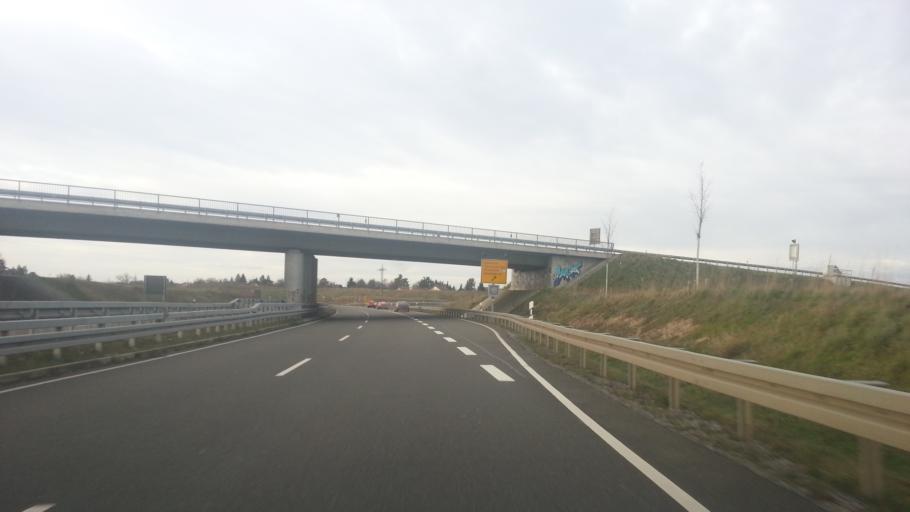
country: DE
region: Baden-Wuerttemberg
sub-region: Karlsruhe Region
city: Plankstadt
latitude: 49.3831
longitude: 8.5963
